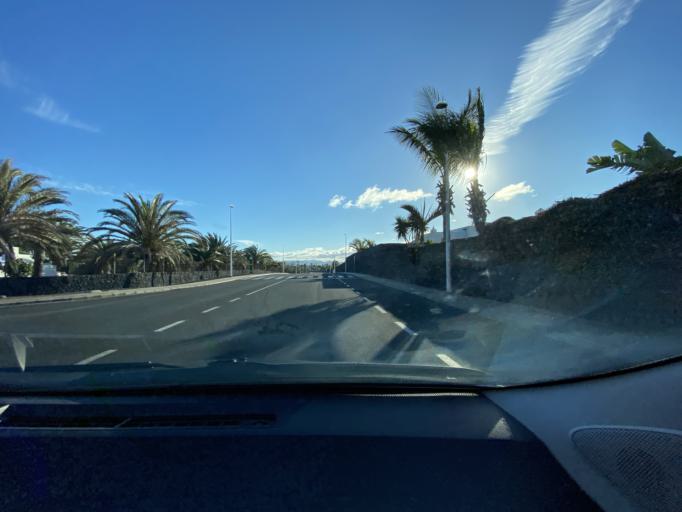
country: ES
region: Canary Islands
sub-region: Provincia de Las Palmas
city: Playa Blanca
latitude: 28.8646
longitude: -13.8414
